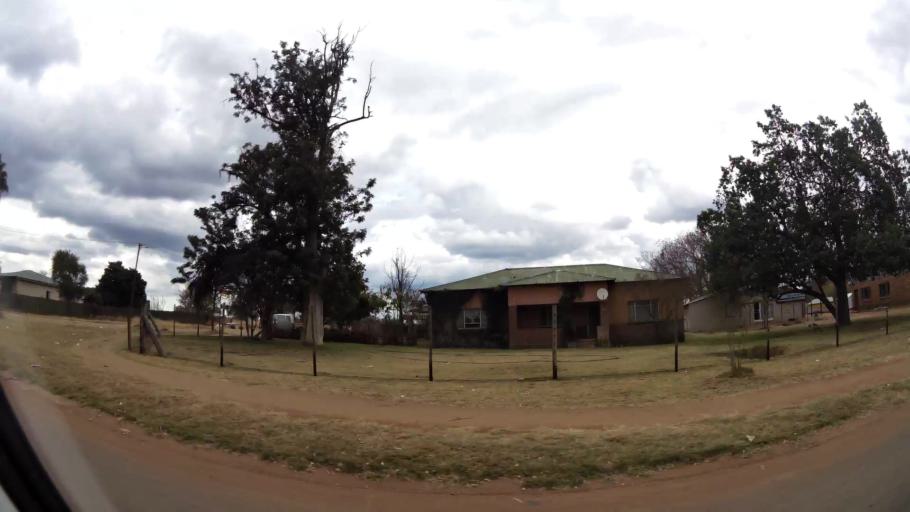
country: ZA
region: Limpopo
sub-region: Waterberg District Municipality
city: Modimolle
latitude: -24.7070
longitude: 28.4177
